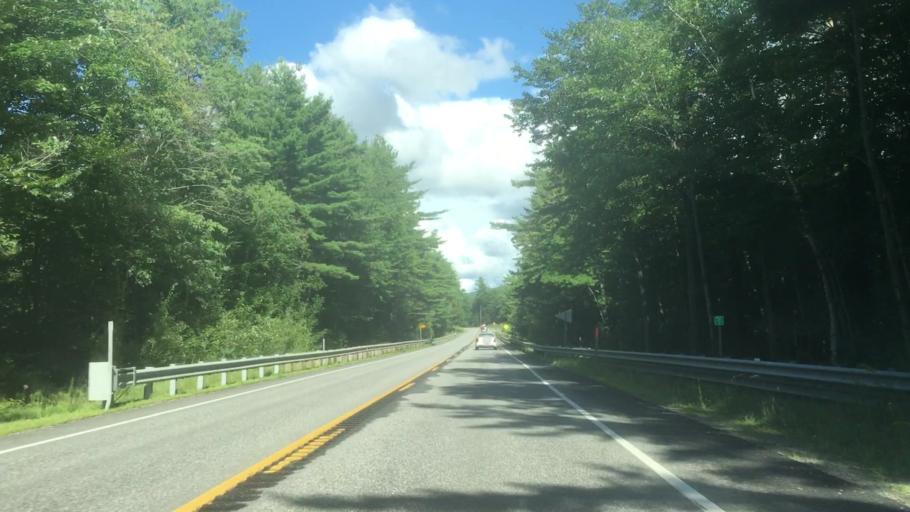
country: US
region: New Hampshire
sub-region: Cheshire County
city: Harrisville
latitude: 43.0369
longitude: -72.0869
